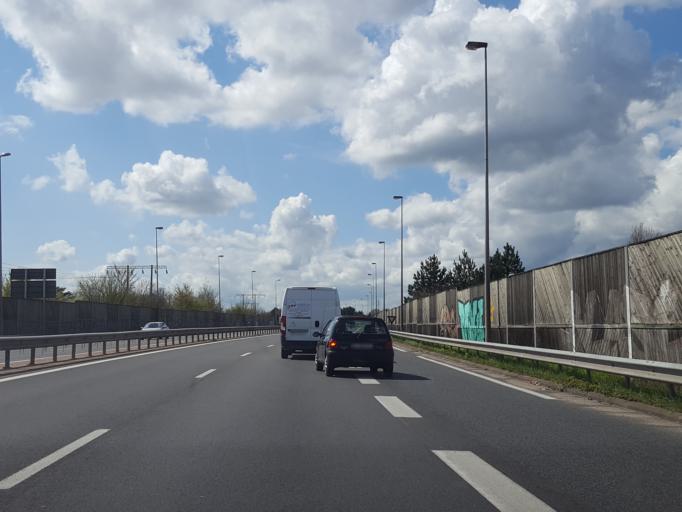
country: FR
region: Centre
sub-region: Departement du Loiret
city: Saran
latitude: 47.9343
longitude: 1.8847
